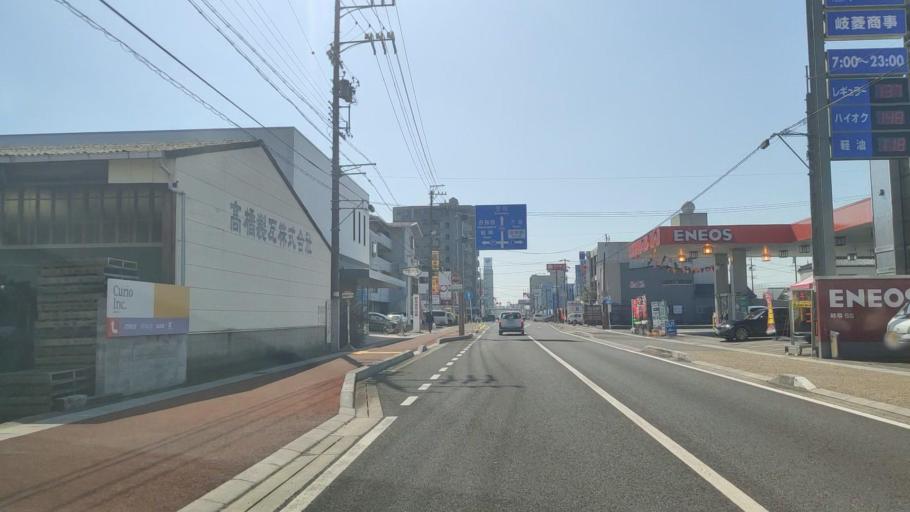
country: JP
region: Gifu
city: Gifu-shi
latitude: 35.3988
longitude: 136.7657
